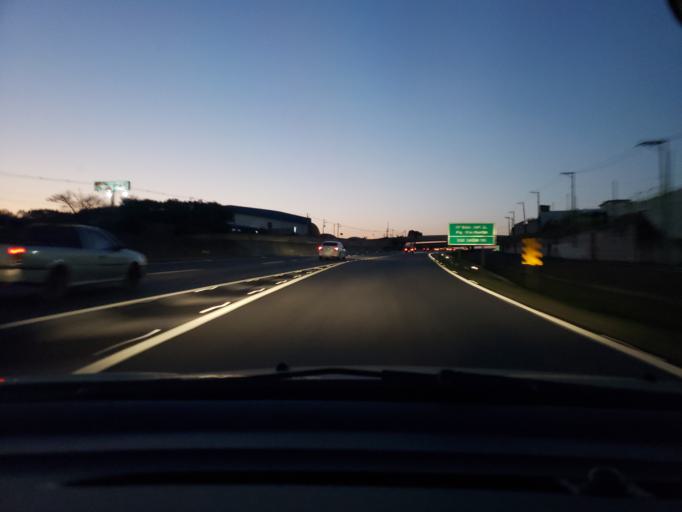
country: BR
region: Sao Paulo
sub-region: Campinas
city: Campinas
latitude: -22.9032
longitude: -47.1082
